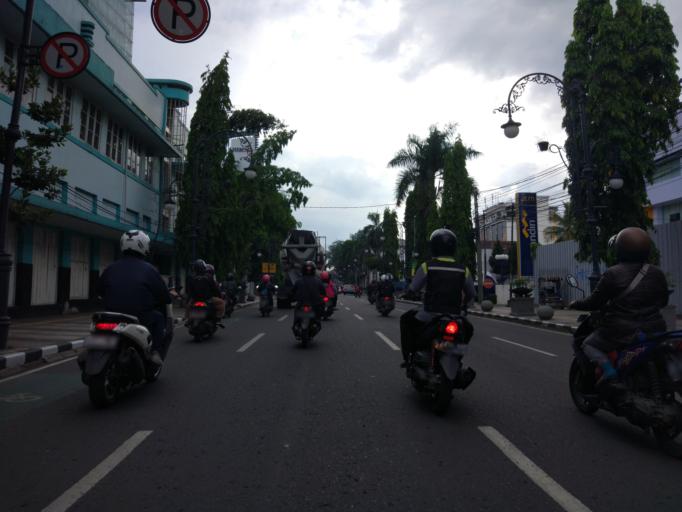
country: ID
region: West Java
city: Bandung
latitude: -6.9220
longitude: 107.6138
